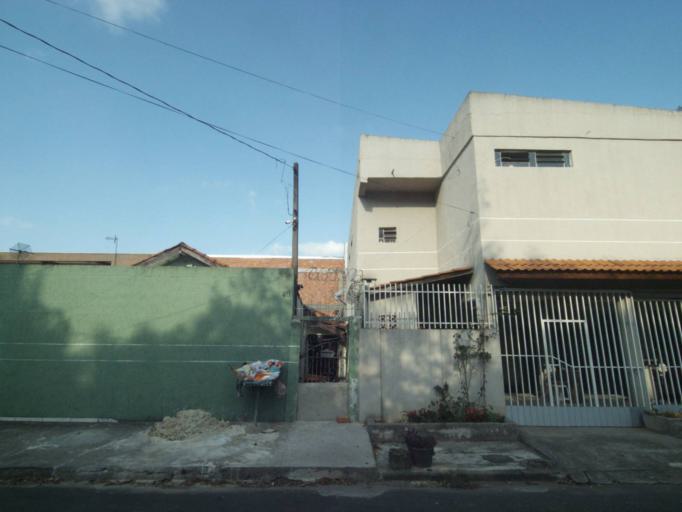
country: BR
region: Parana
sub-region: Curitiba
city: Curitiba
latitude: -25.4941
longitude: -49.3359
